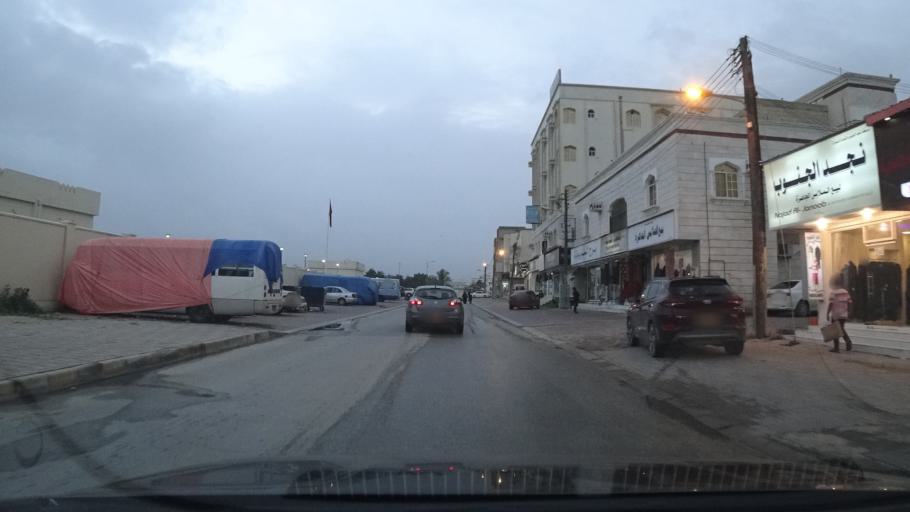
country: OM
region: Zufar
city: Salalah
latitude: 17.0091
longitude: 54.0781
